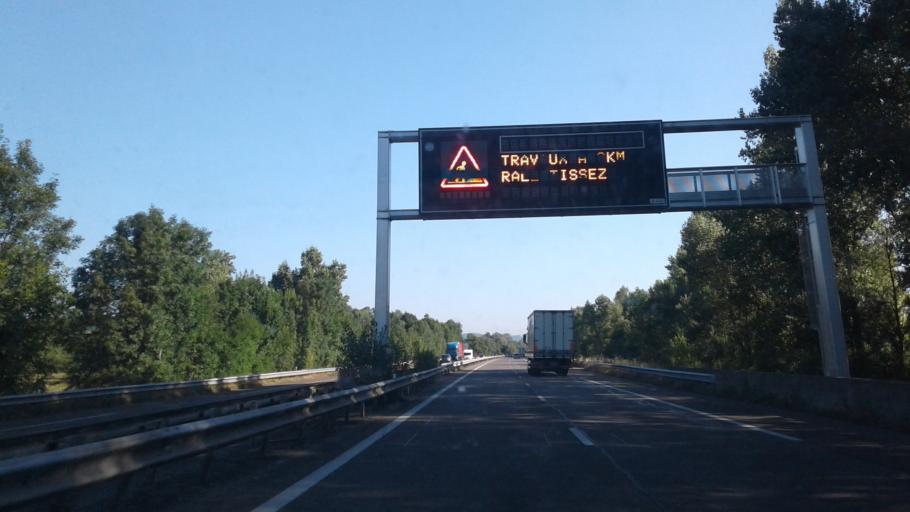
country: FR
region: Rhone-Alpes
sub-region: Departement de l'Ain
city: Priay
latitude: 46.0193
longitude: 5.3134
